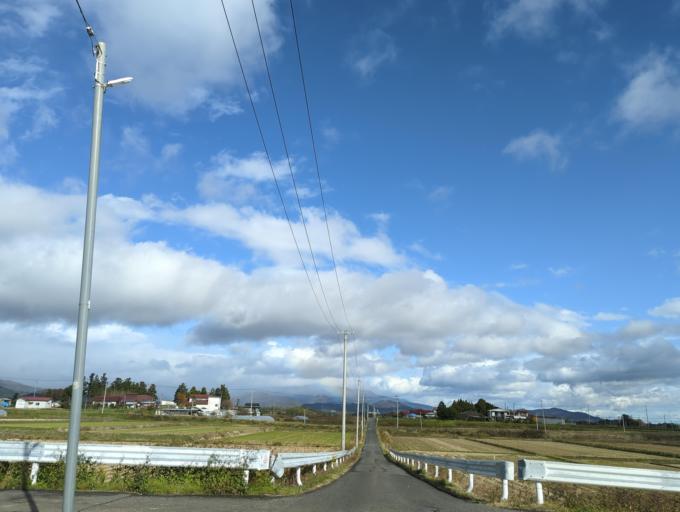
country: JP
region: Fukushima
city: Koriyama
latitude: 37.4080
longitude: 140.3148
